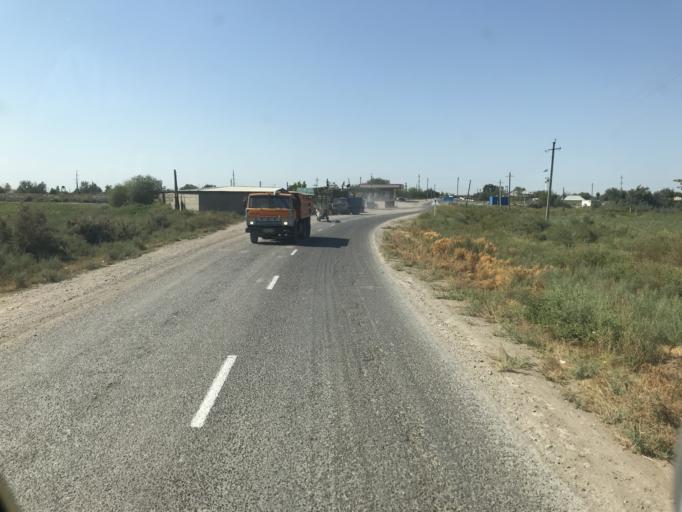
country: KZ
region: Ongtustik Qazaqstan
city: Myrzakent
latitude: 40.6713
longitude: 68.5526
